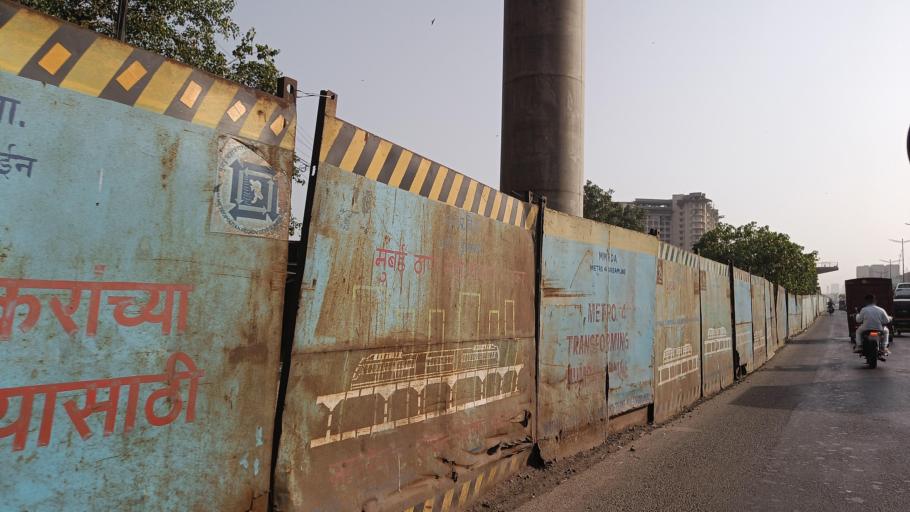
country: IN
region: Maharashtra
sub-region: Mumbai Suburban
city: Mumbai
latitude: 19.0608
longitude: 72.8929
